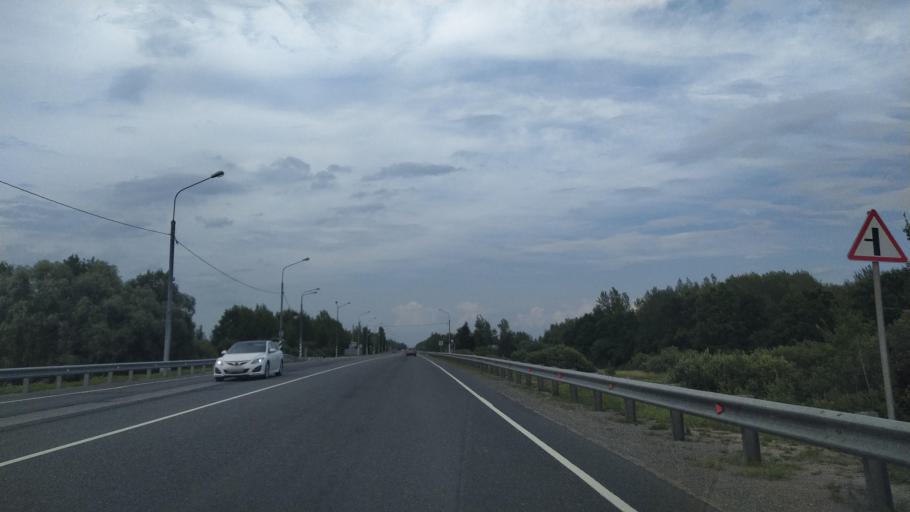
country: RU
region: Novgorod
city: Pankovka
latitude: 58.4492
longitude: 31.1309
